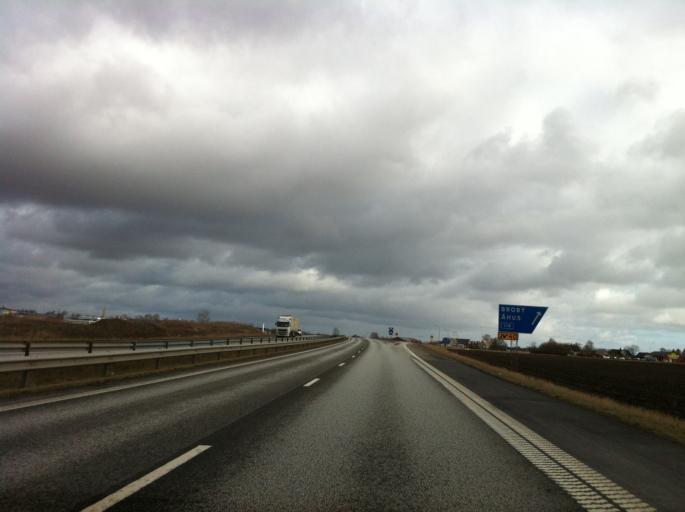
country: SE
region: Skane
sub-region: Kristianstads Kommun
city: Onnestad
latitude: 56.0307
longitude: 14.0781
